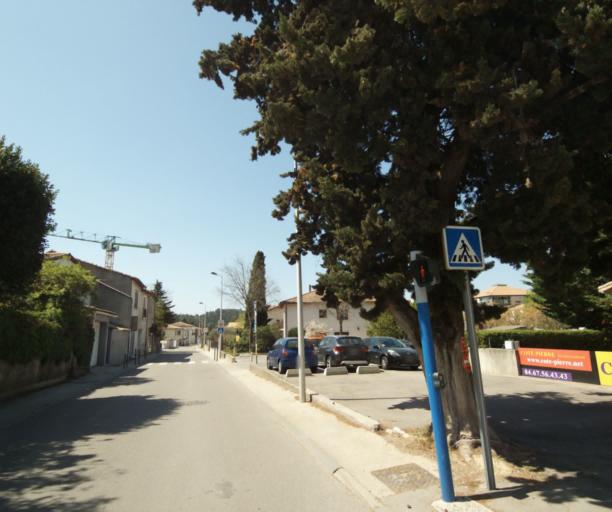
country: FR
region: Languedoc-Roussillon
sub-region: Departement de l'Herault
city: Prades-le-Lez
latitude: 43.6972
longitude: 3.8661
